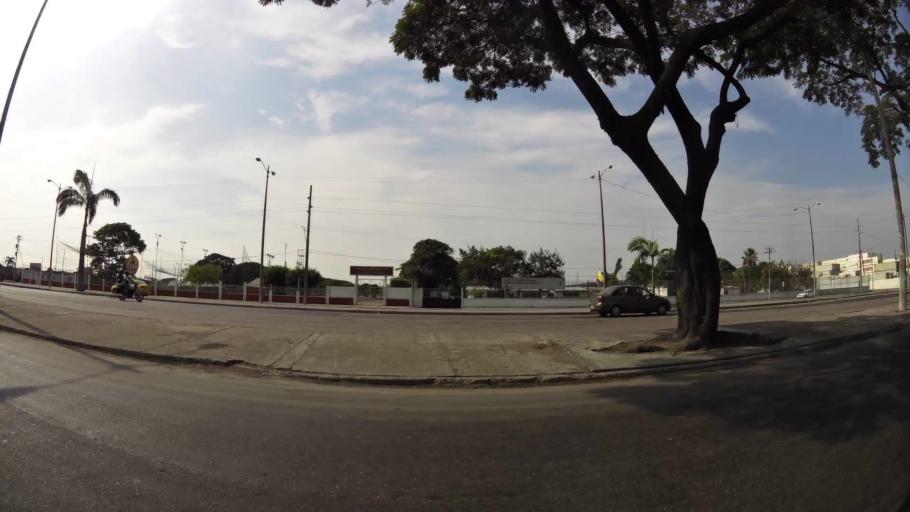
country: EC
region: Guayas
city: Guayaquil
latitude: -2.2665
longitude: -79.9001
